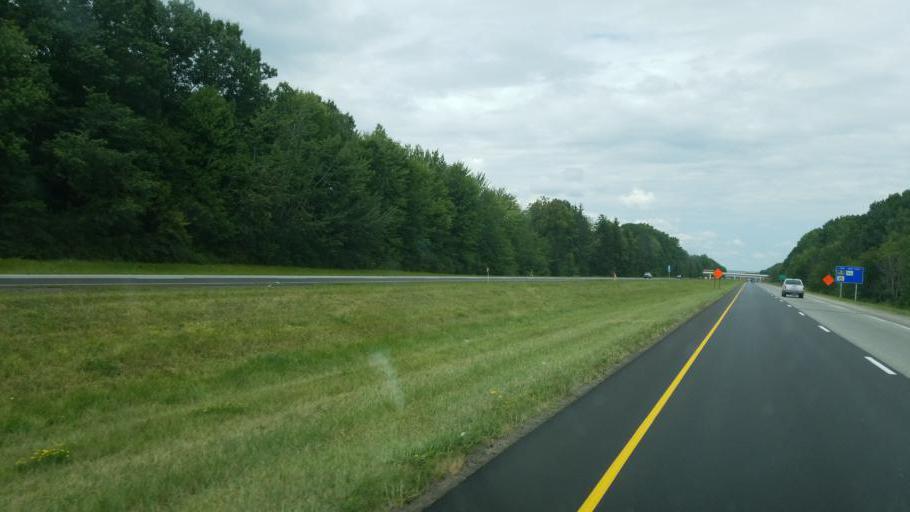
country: US
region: Ohio
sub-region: Mahoning County
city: Austintown
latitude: 41.0764
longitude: -80.7523
